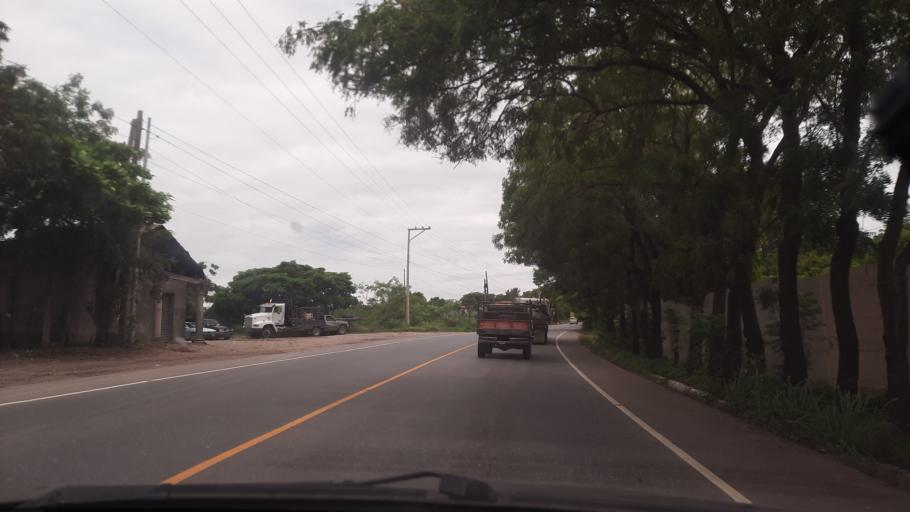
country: GT
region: Zacapa
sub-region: Municipio de Zacapa
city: Gualan
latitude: 15.1314
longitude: -89.3473
